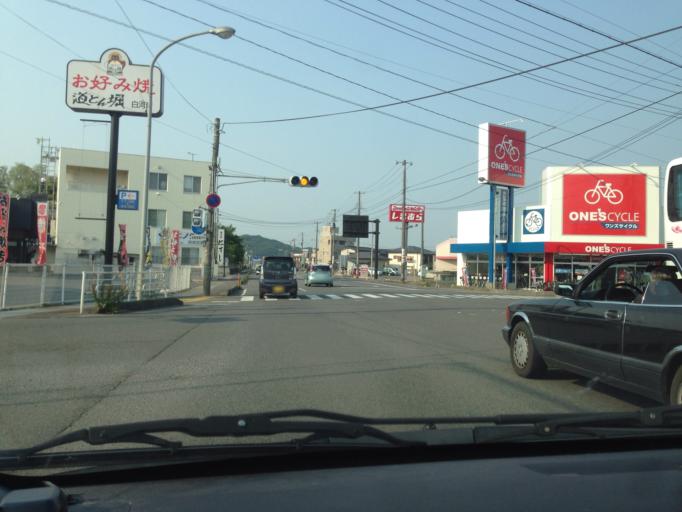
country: JP
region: Tochigi
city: Kuroiso
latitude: 37.1255
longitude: 140.1969
